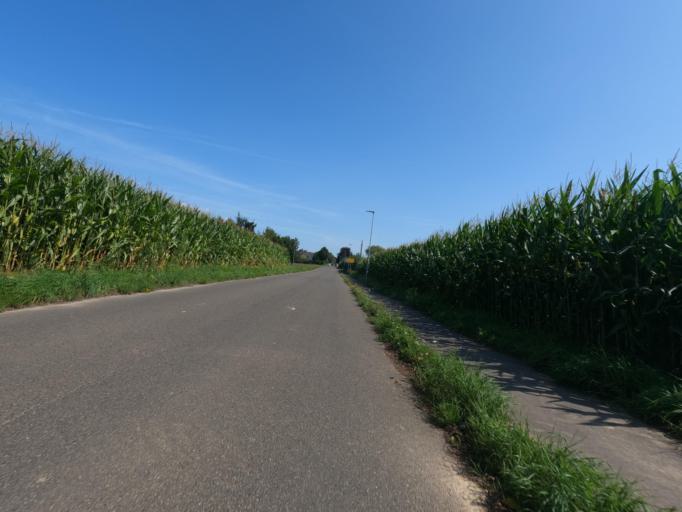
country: DE
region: North Rhine-Westphalia
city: Baesweiler
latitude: 50.9192
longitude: 6.1931
